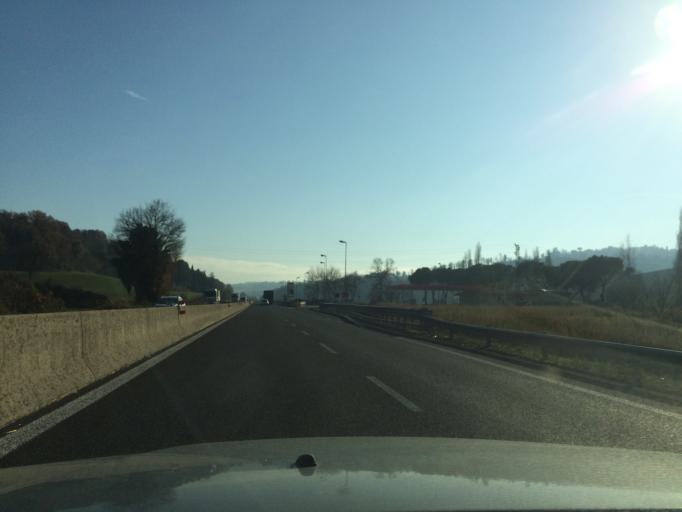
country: IT
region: Umbria
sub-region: Provincia di Perugia
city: Todi
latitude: 42.7735
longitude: 12.4472
